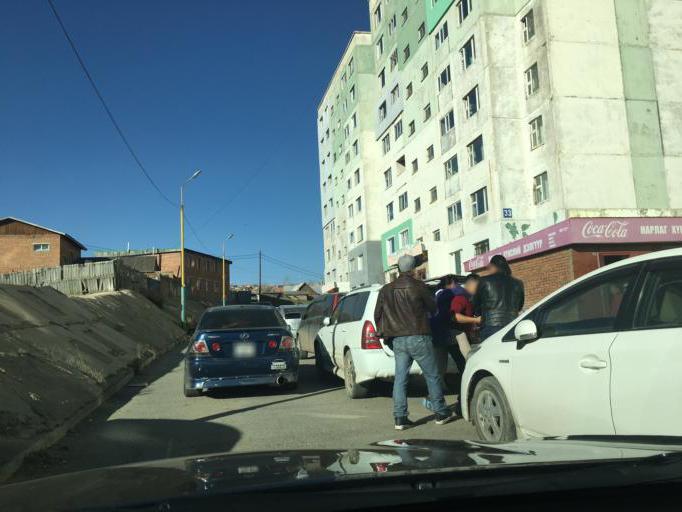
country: MN
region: Ulaanbaatar
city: Ulaanbaatar
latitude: 47.9260
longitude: 106.8680
